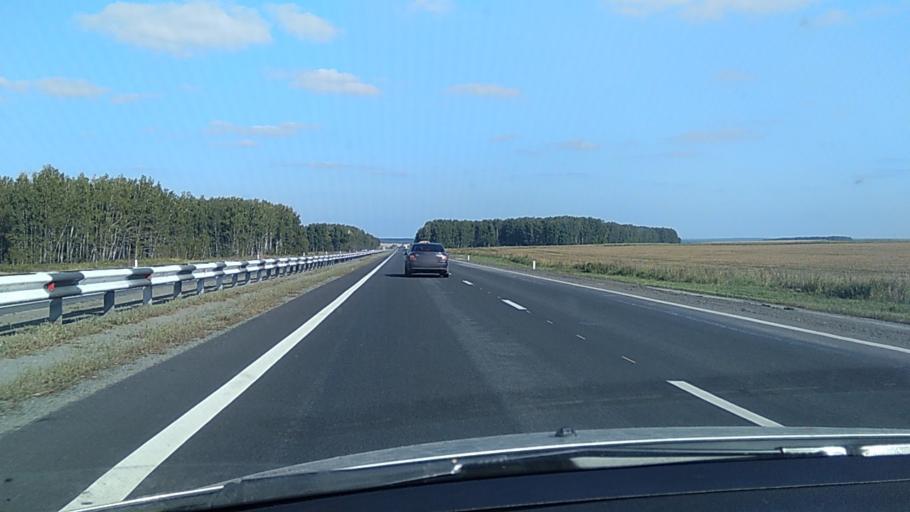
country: RU
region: Chelyabinsk
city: Timiryazevskiy
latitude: 54.9522
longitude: 60.8788
